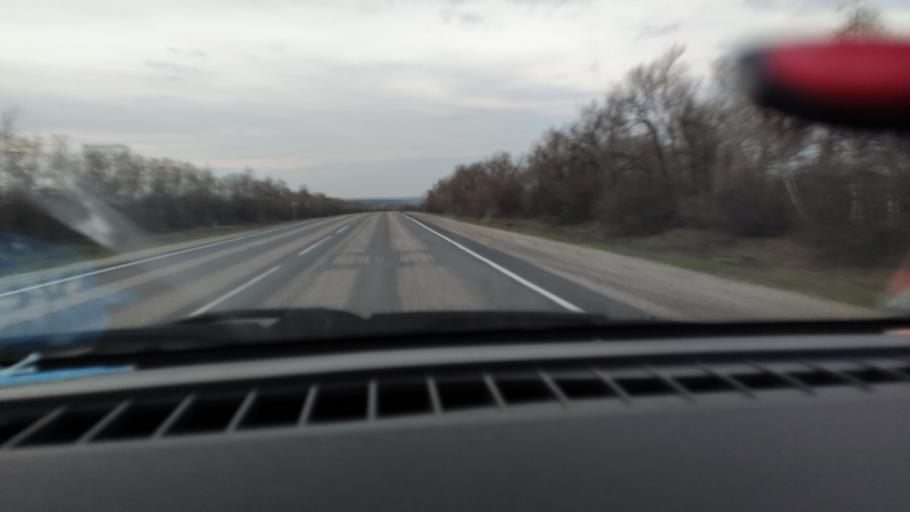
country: RU
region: Saratov
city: Sinodskoye
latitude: 51.9542
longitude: 46.6126
